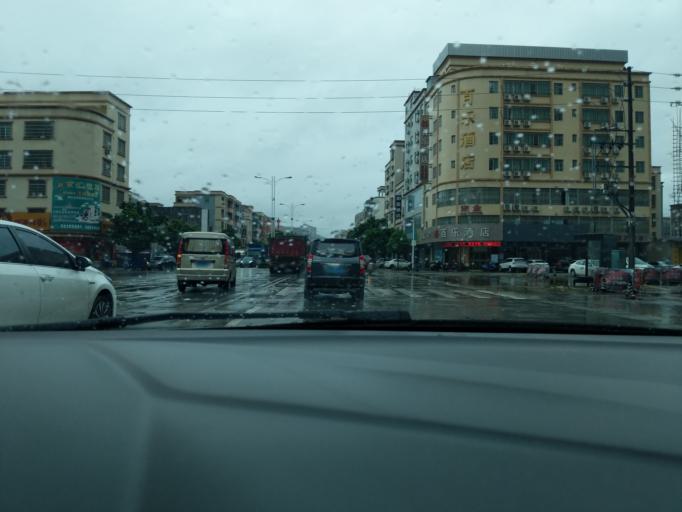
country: CN
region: Guangdong
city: Pingshi
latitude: 22.1965
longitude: 112.3342
